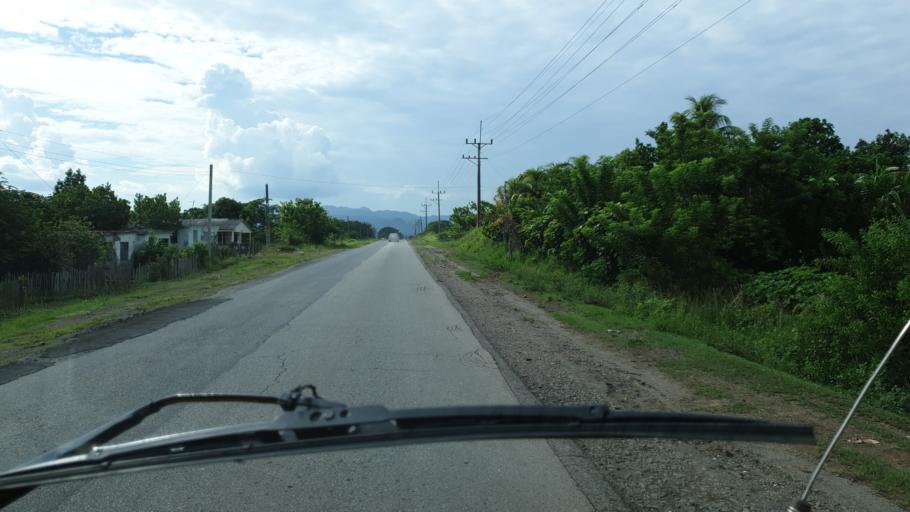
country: CU
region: Cienfuegos
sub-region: Municipio de Cienfuegos
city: Cumanayagua
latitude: 22.0735
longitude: -80.3090
